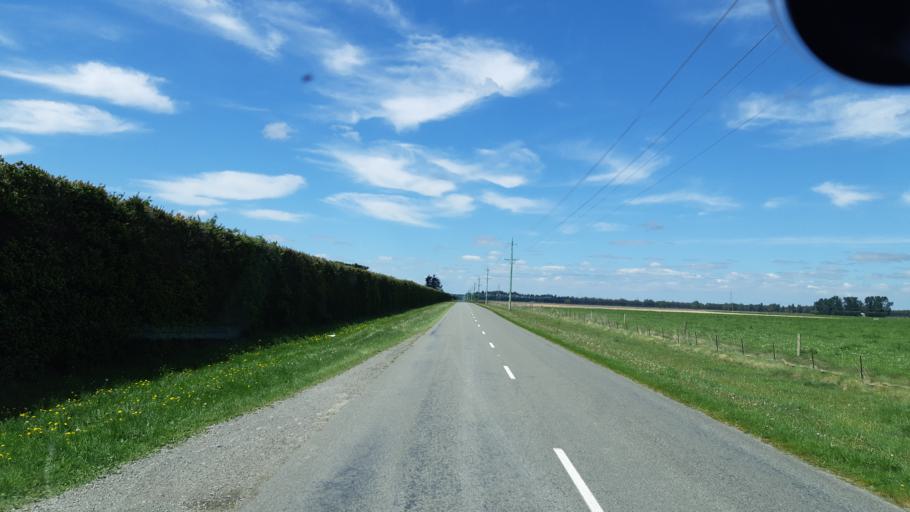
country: NZ
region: Canterbury
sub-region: Ashburton District
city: Methven
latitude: -43.7212
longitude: 171.4721
